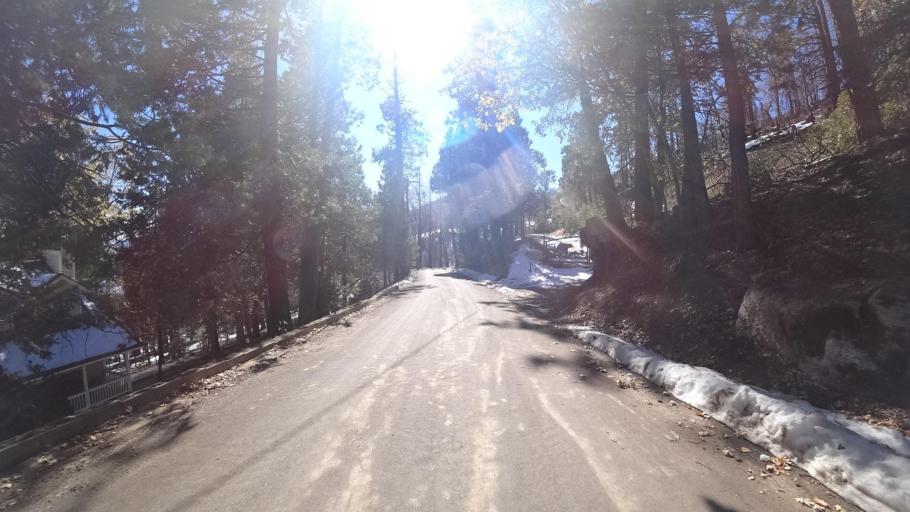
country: US
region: California
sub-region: Kern County
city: Alta Sierra
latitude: 35.7249
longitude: -118.5488
